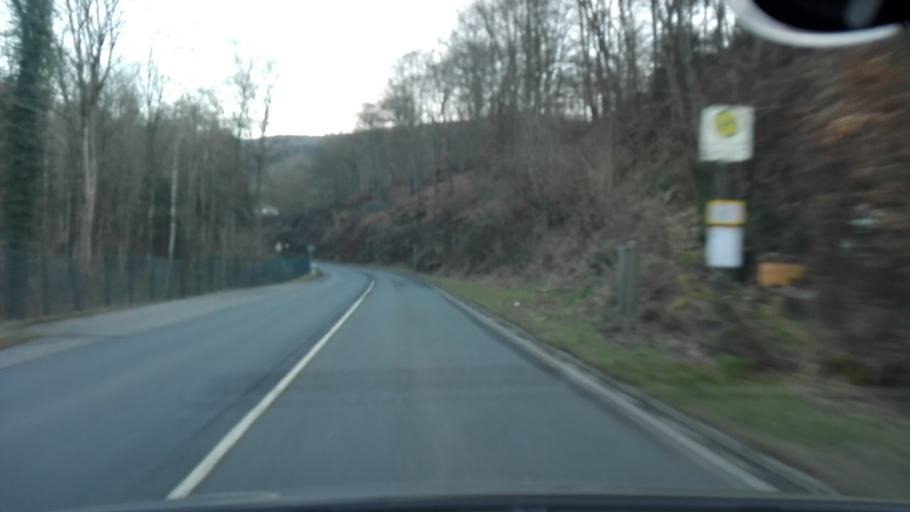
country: DE
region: North Rhine-Westphalia
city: Plettenberg
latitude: 51.2244
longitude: 7.9015
